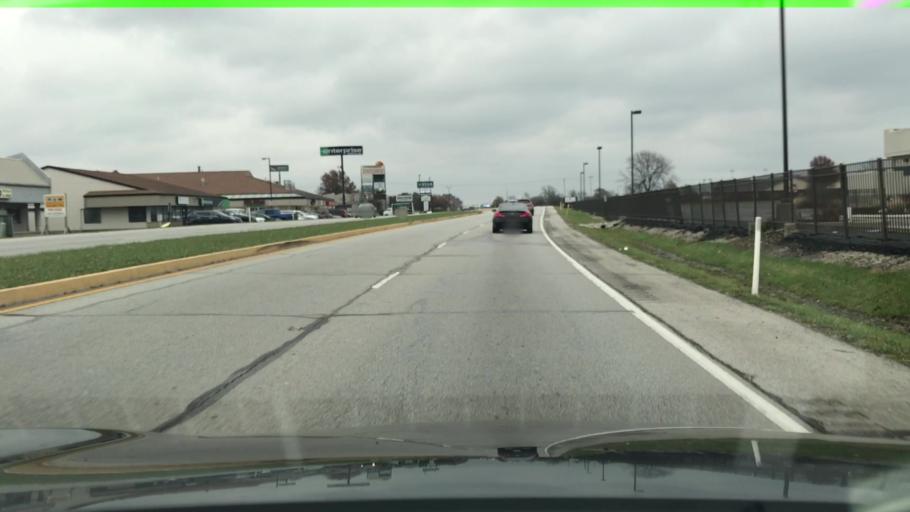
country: US
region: Indiana
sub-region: Delaware County
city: Muncie
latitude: 40.2191
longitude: -85.4284
